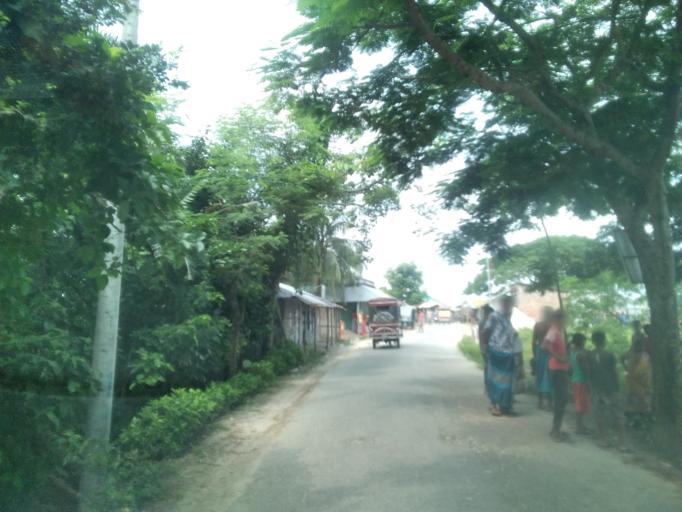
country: BD
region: Khulna
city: Phultala
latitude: 22.7001
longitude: 89.4541
